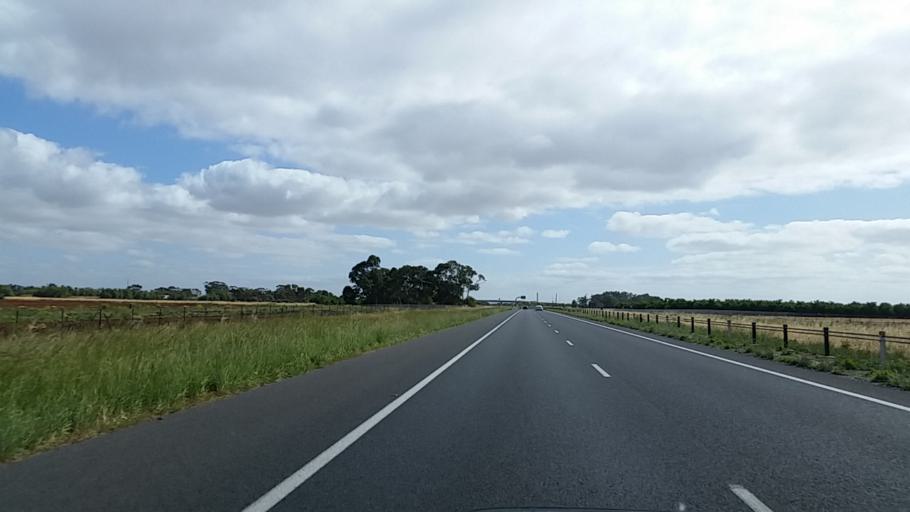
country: AU
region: South Australia
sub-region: Playford
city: Angle Vale
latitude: -34.6455
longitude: 138.6657
